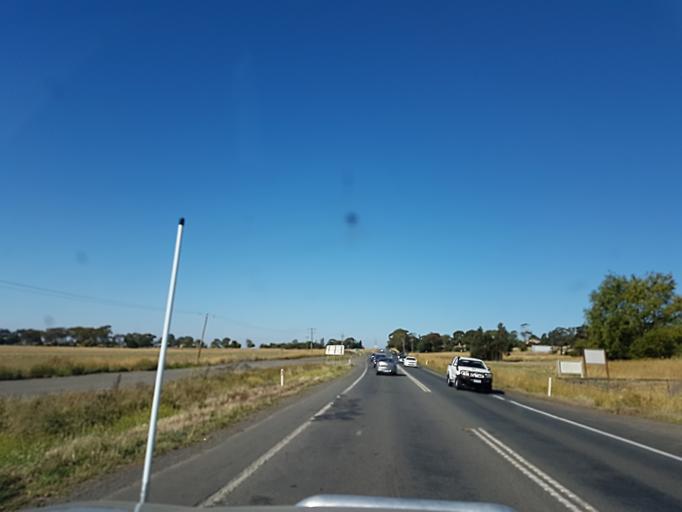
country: AU
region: Victoria
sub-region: Colac-Otway
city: Colac
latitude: -38.3265
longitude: 143.6245
